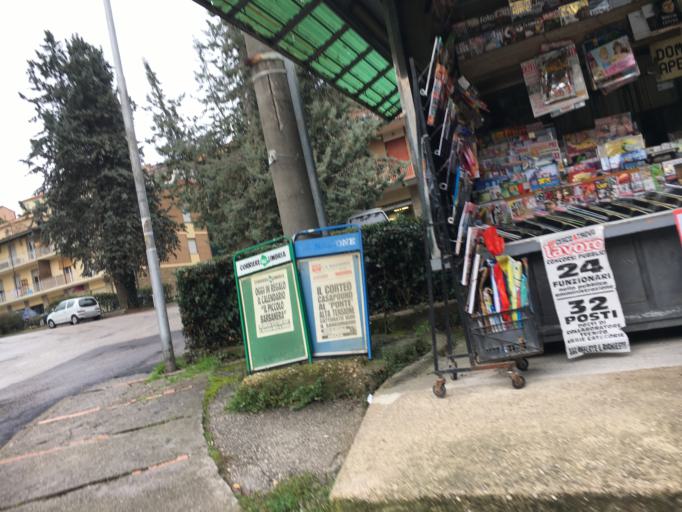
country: IT
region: Umbria
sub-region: Provincia di Perugia
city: Perugia
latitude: 43.1165
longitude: 12.3746
